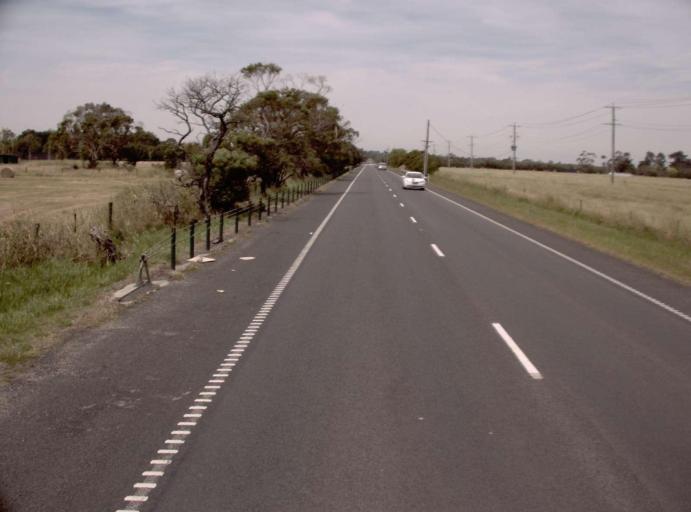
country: AU
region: Victoria
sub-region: Mornington Peninsula
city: Langwarrin South
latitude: -38.2183
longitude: 145.2188
